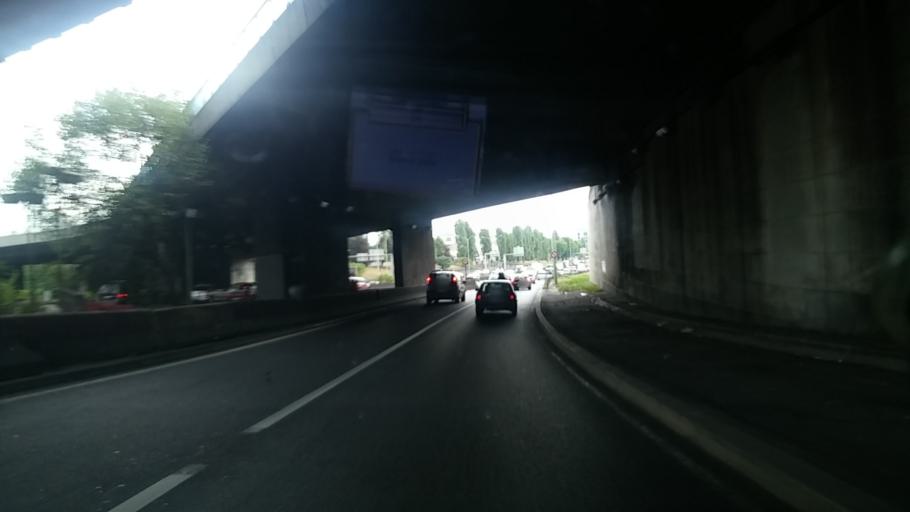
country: FR
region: Ile-de-France
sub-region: Departement de Seine-Saint-Denis
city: Bagnolet
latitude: 48.8645
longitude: 2.4127
